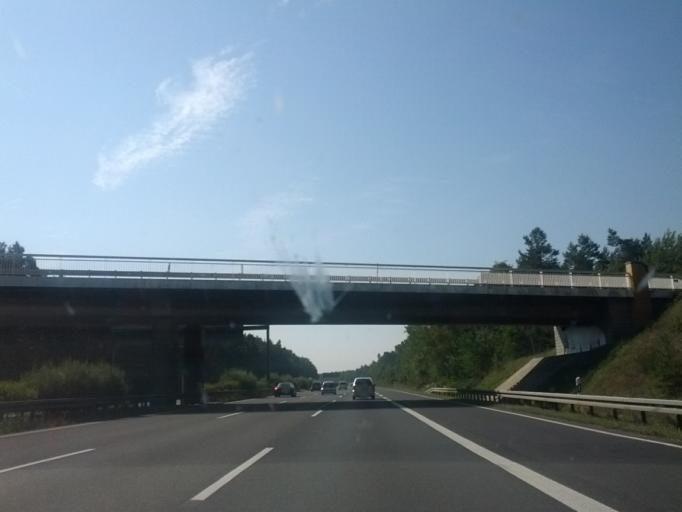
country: DE
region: Brandenburg
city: Fichtenwalde
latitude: 52.2697
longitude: 12.9092
